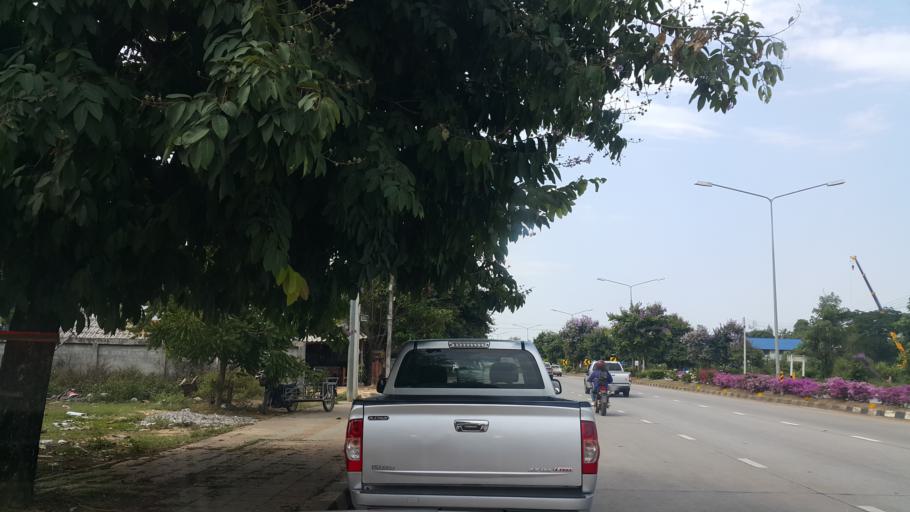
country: TH
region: Chiang Rai
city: Chiang Rai
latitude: 19.9210
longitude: 99.8614
